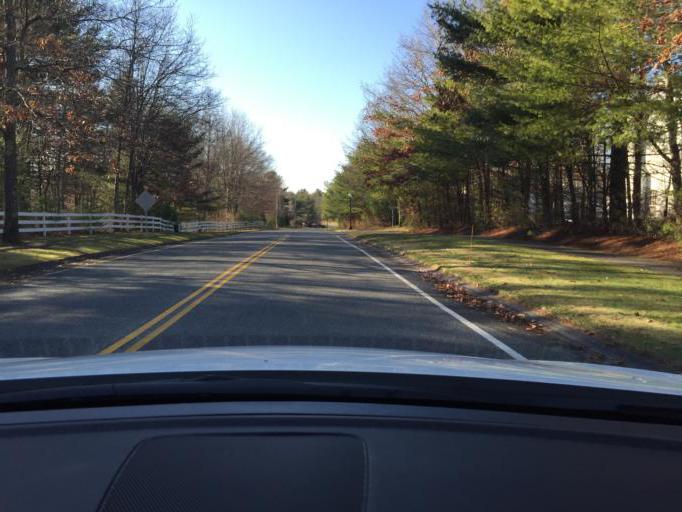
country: US
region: Massachusetts
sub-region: Bristol County
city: Mansfield
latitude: 42.0722
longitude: -71.2055
